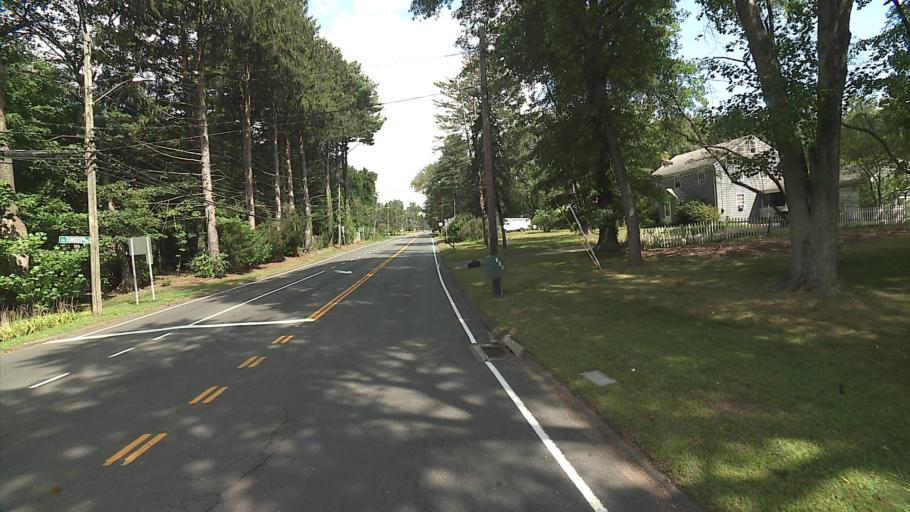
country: US
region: Connecticut
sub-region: Hartford County
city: Blue Hills
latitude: 41.8437
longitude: -72.7445
